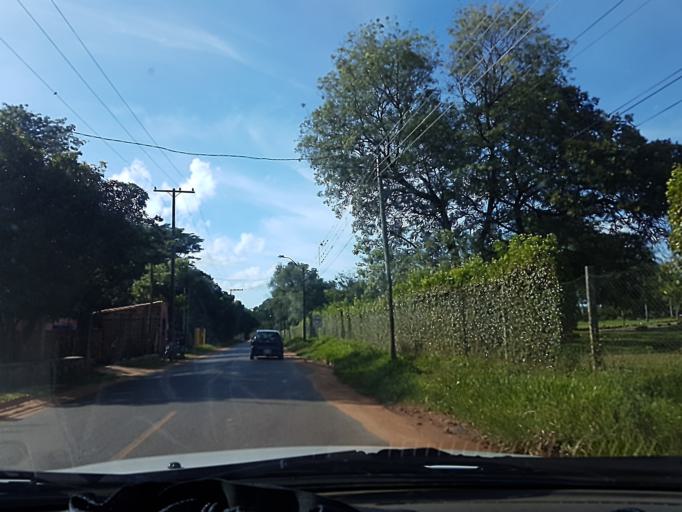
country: PY
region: Central
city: Limpio
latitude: -25.1928
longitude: -57.4614
